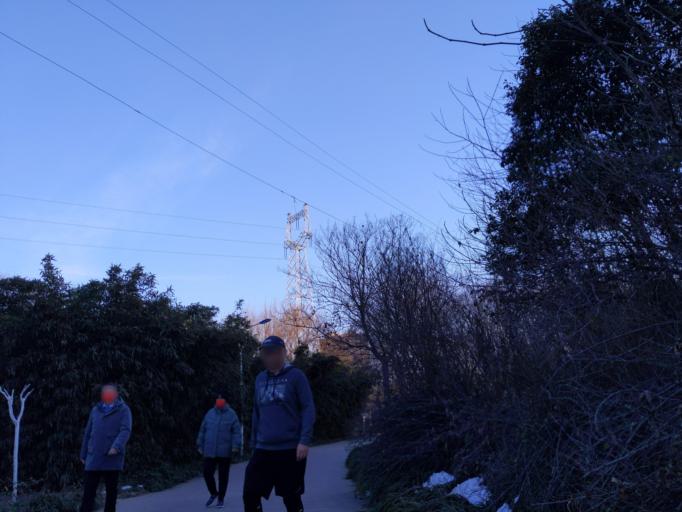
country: CN
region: Henan Sheng
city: Puyang
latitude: 35.7652
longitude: 115.0012
